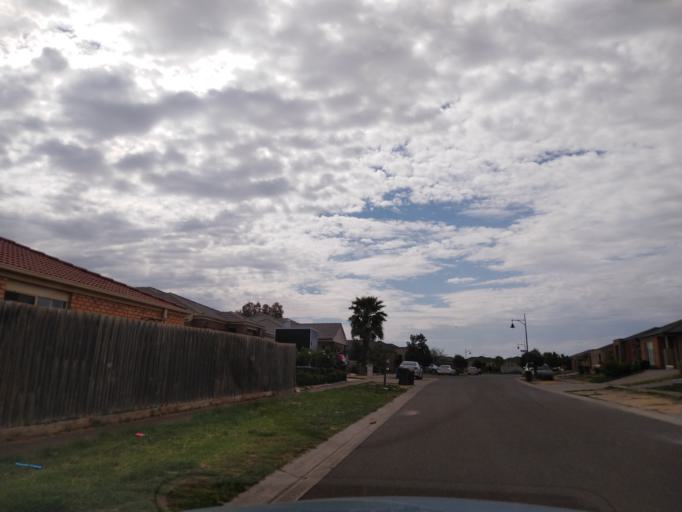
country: AU
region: Victoria
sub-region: Wyndham
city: Williams Landing
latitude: -37.8475
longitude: 144.7174
